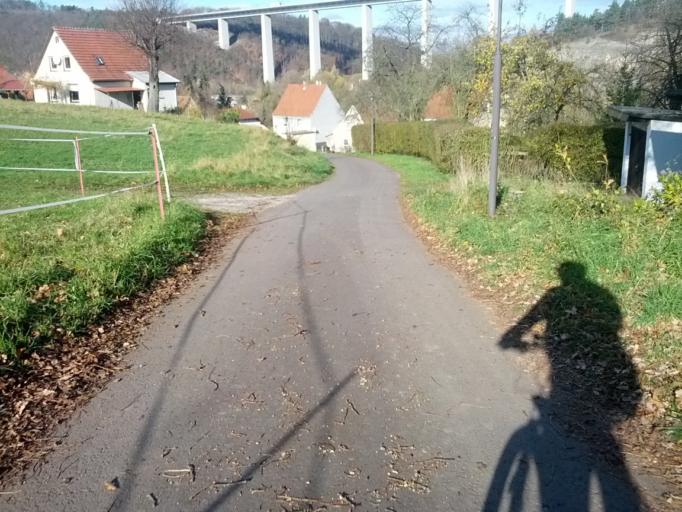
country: DE
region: Thuringia
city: Krauthausen
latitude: 51.0051
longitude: 10.2333
